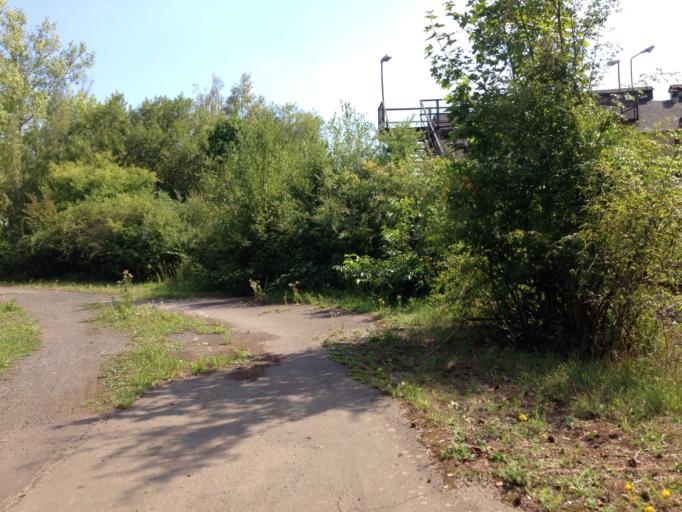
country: DE
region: Hesse
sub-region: Regierungsbezirk Giessen
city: Giessen
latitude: 50.5686
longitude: 8.6855
